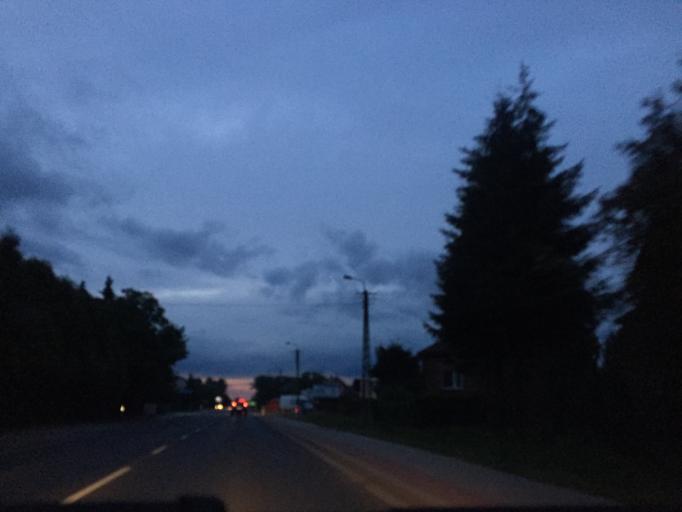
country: PL
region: Lesser Poland Voivodeship
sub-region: Powiat oswiecimski
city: Zaborze
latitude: 50.0265
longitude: 19.2531
